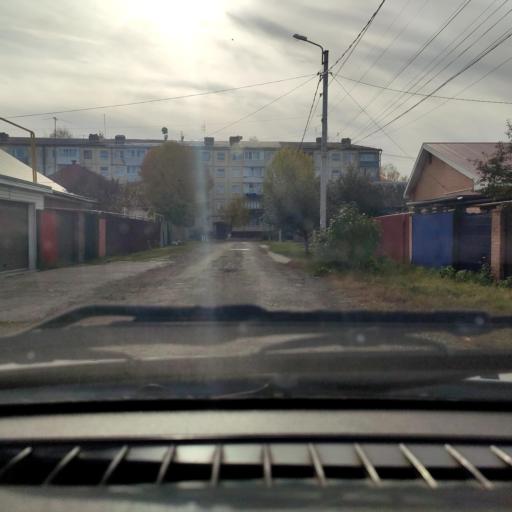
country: RU
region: Samara
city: Tol'yatti
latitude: 53.5331
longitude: 49.4229
